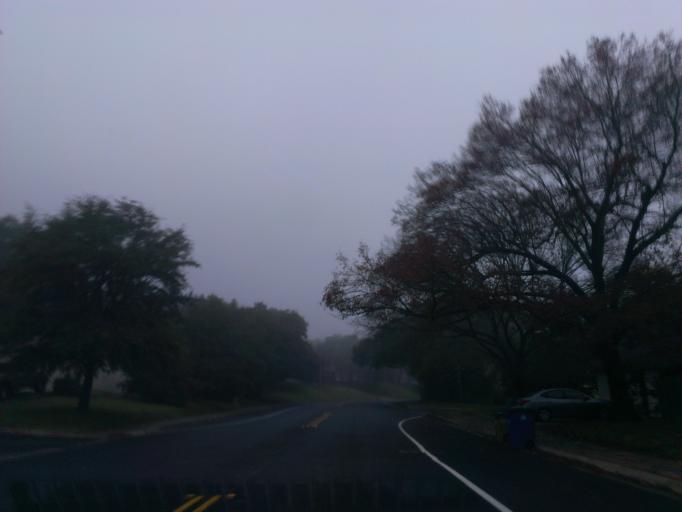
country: US
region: Texas
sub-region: Williamson County
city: Jollyville
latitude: 30.3736
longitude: -97.7891
